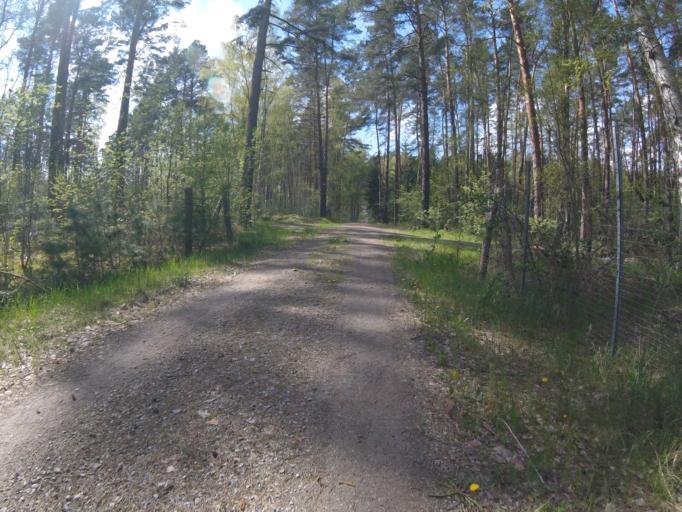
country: DE
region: Brandenburg
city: Gross Koris
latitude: 52.2118
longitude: 13.7287
